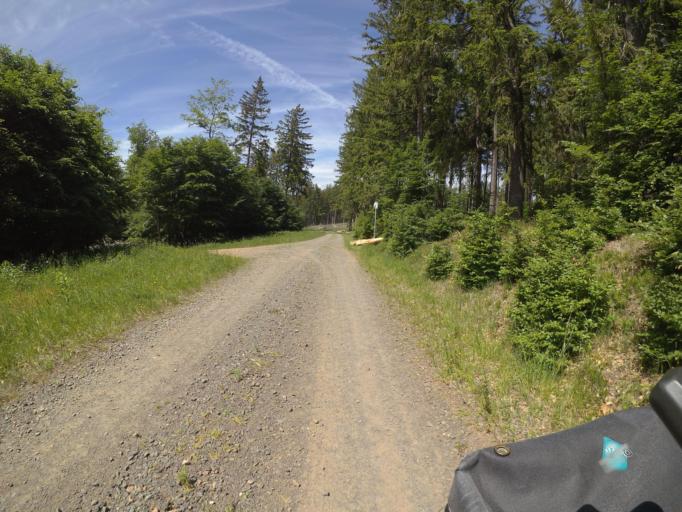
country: DE
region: Rheinland-Pfalz
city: Deuselbach
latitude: 49.7534
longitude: 7.0936
